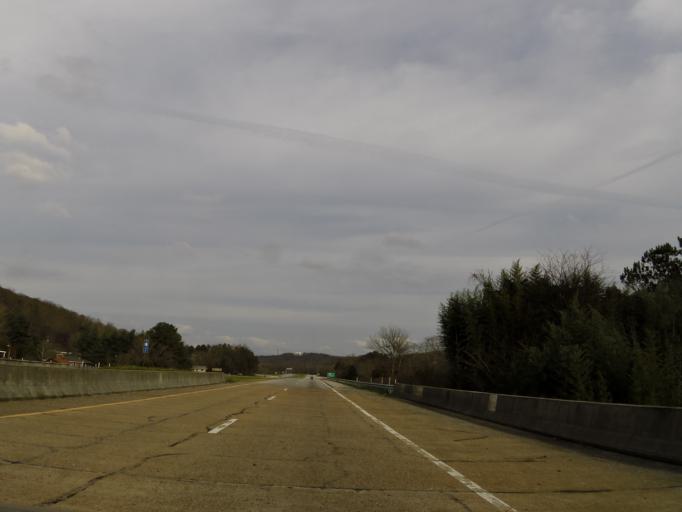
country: US
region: Tennessee
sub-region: Hamilton County
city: Falling Water
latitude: 35.1848
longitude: -85.2541
